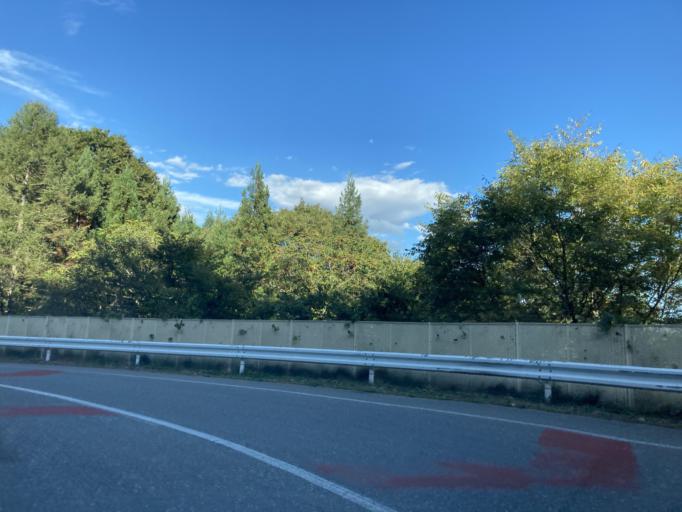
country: JP
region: Nagano
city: Omachi
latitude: 36.4862
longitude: 137.9024
